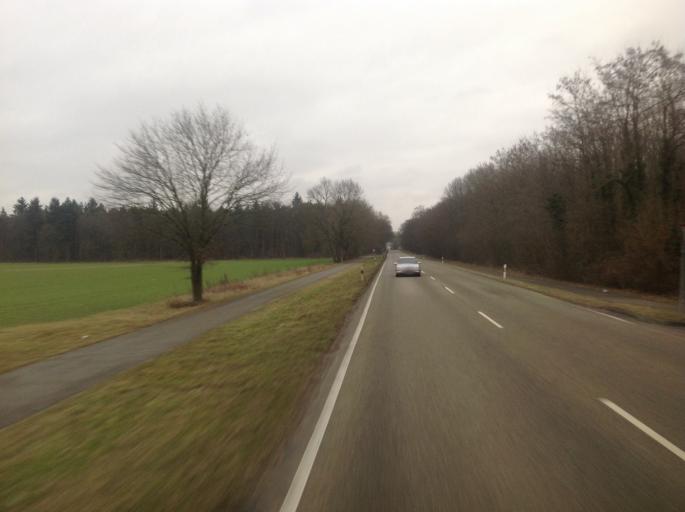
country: DE
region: Baden-Wuerttemberg
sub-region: Karlsruhe Region
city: Hugelsheim
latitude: 48.8043
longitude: 8.1281
